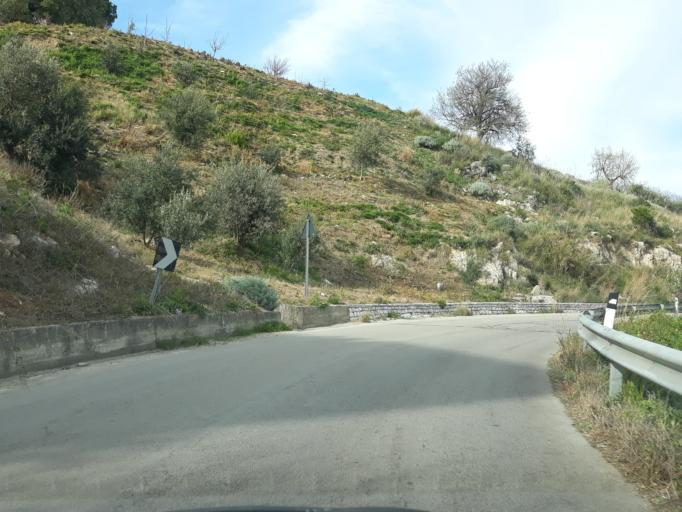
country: IT
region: Sicily
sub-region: Palermo
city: Altofonte
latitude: 38.0417
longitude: 13.3091
